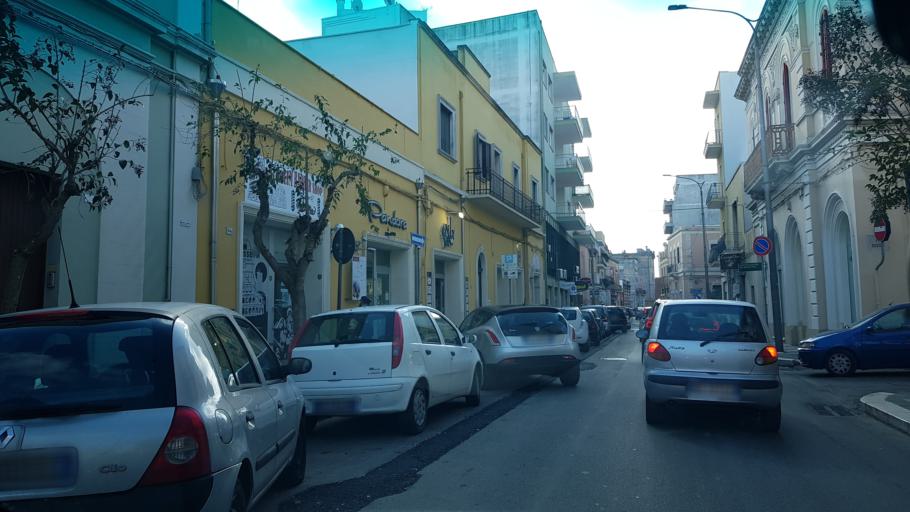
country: IT
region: Apulia
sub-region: Provincia di Brindisi
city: San Pietro Vernotico
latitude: 40.4896
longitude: 17.9968
